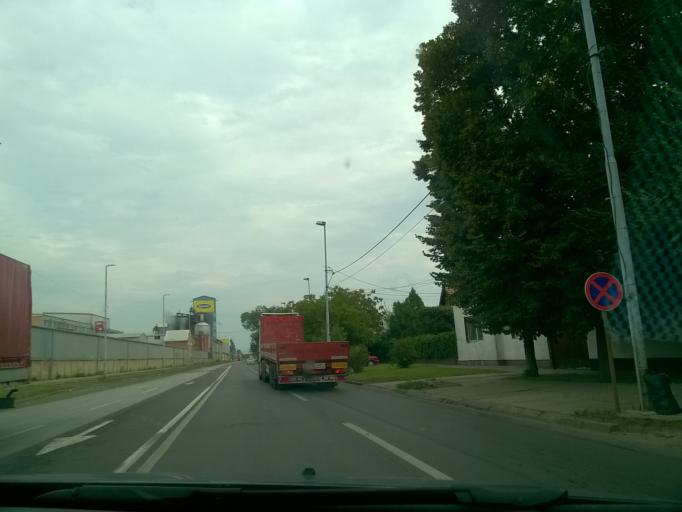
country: RS
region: Autonomna Pokrajina Vojvodina
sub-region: Srednjebanatski Okrug
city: Zrenjanin
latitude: 45.3832
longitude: 20.4162
